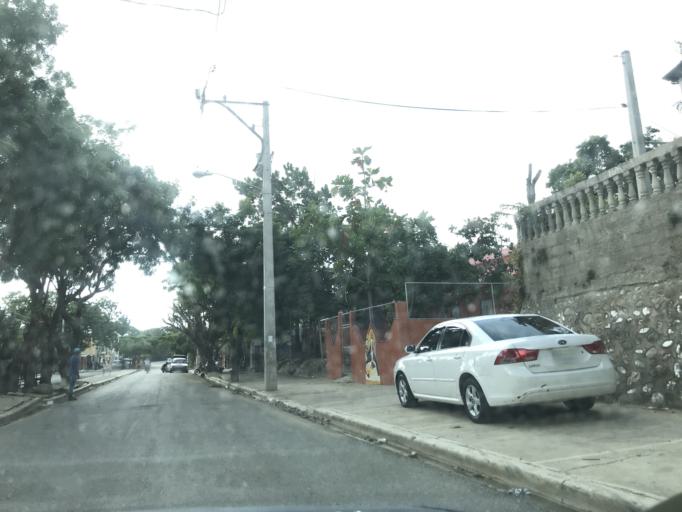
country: DO
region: Santiago
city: Santiago de los Caballeros
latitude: 19.4491
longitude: -70.7323
